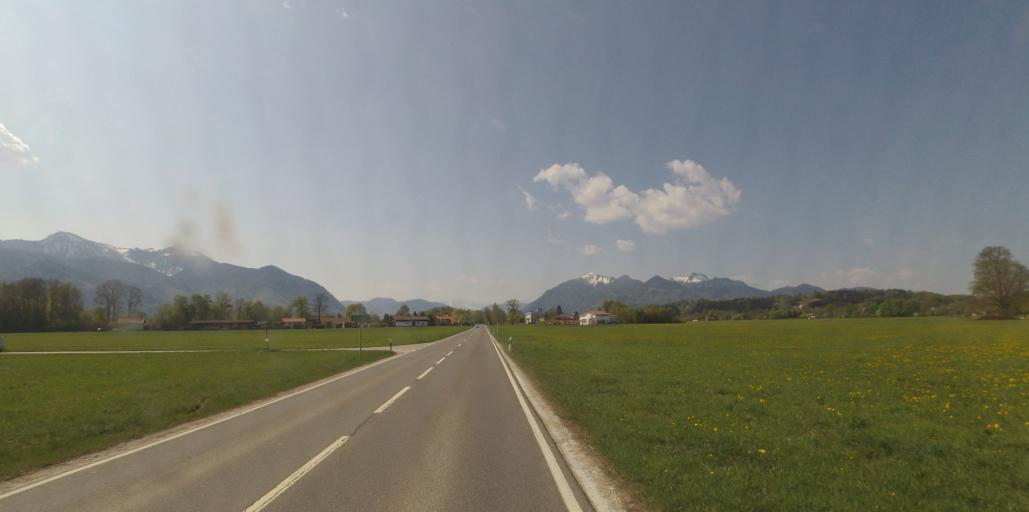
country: DE
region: Bavaria
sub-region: Upper Bavaria
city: Ubersee
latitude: 47.8171
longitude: 12.4947
